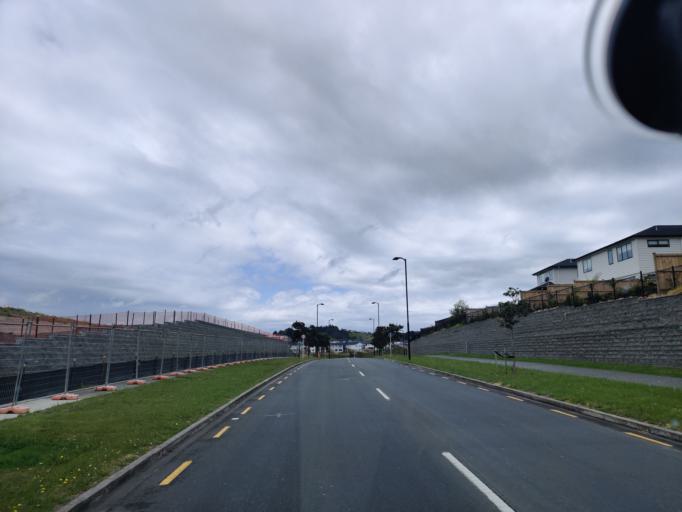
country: NZ
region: Auckland
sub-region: Auckland
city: Rothesay Bay
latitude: -36.5945
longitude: 174.6710
